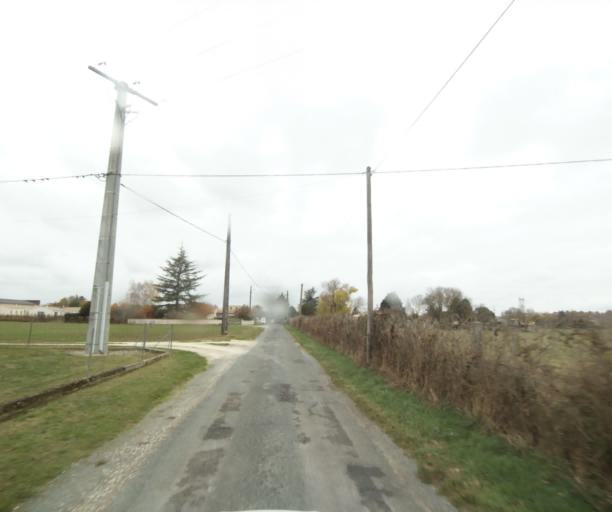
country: FR
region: Poitou-Charentes
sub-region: Departement de la Charente-Maritime
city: Bussac-sur-Charente
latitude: 45.7677
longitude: -0.6314
